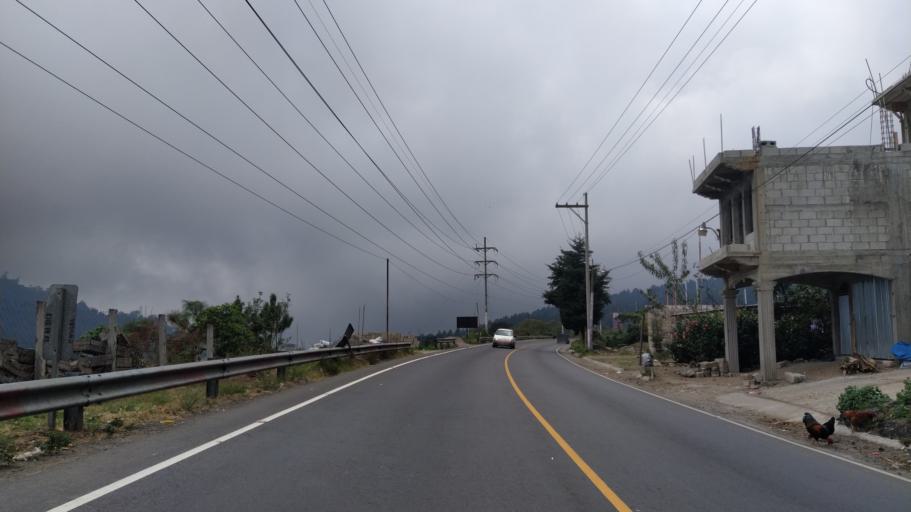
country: GT
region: Quetzaltenango
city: Zunil
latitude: 14.7472
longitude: -91.5114
